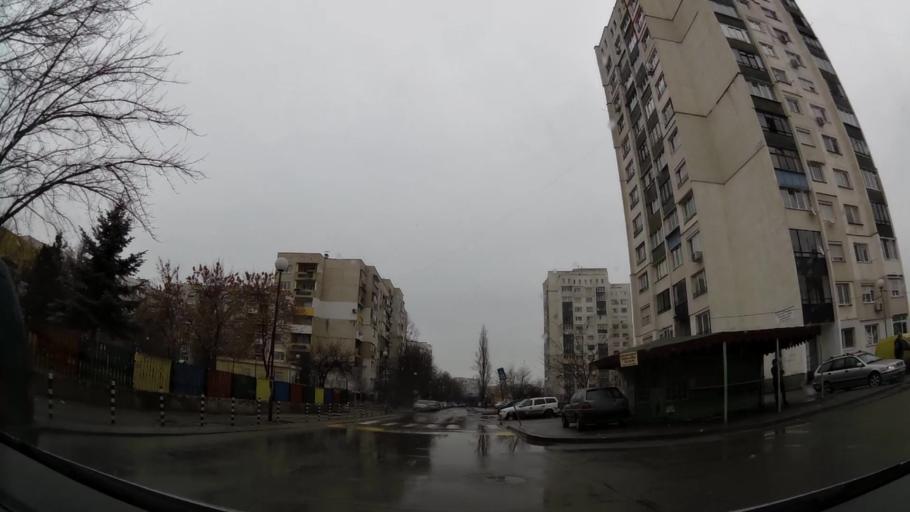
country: BG
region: Sofia-Capital
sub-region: Stolichna Obshtina
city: Sofia
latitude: 42.6524
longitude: 23.4006
